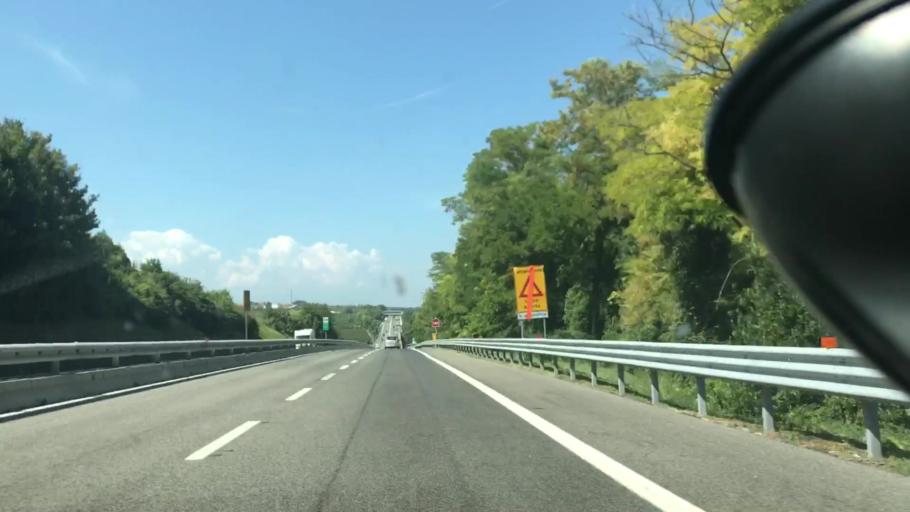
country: IT
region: Abruzzo
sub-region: Provincia di Chieti
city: Tollo
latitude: 42.3595
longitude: 14.3452
